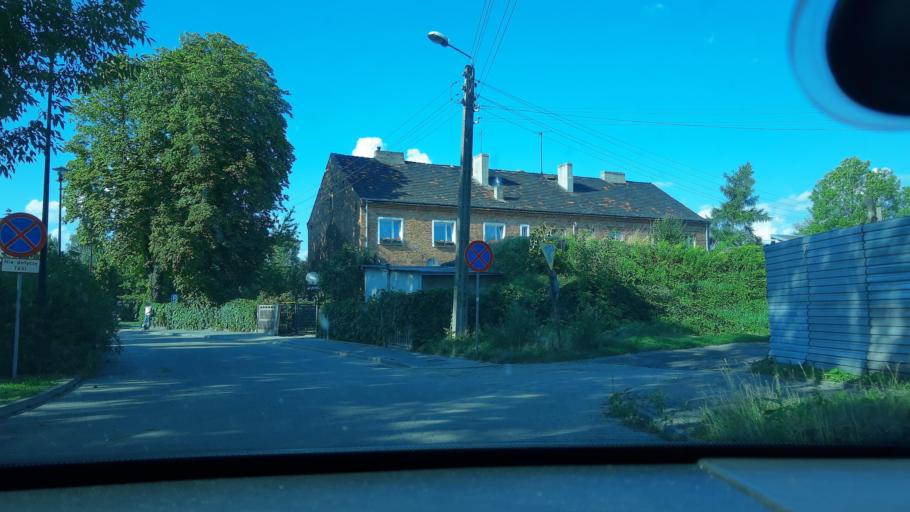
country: PL
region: Lodz Voivodeship
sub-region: Powiat sieradzki
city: Sieradz
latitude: 51.5968
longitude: 18.7152
